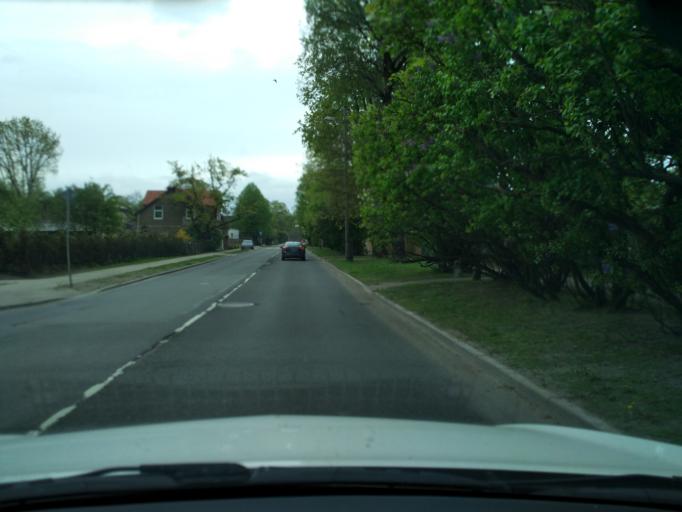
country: LV
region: Marupe
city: Marupe
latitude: 56.9176
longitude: 24.0738
